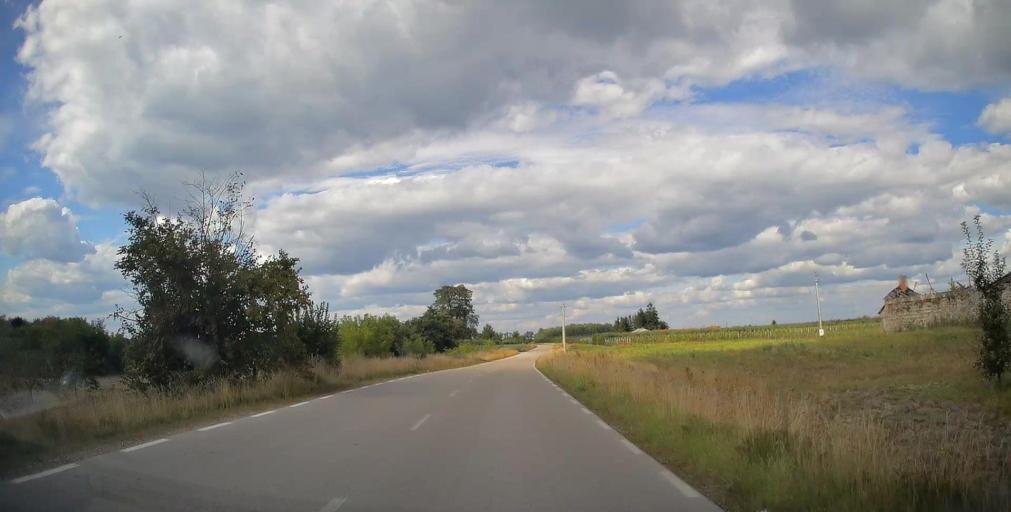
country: PL
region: Masovian Voivodeship
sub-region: Powiat grojecki
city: Goszczyn
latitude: 51.7549
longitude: 20.9027
